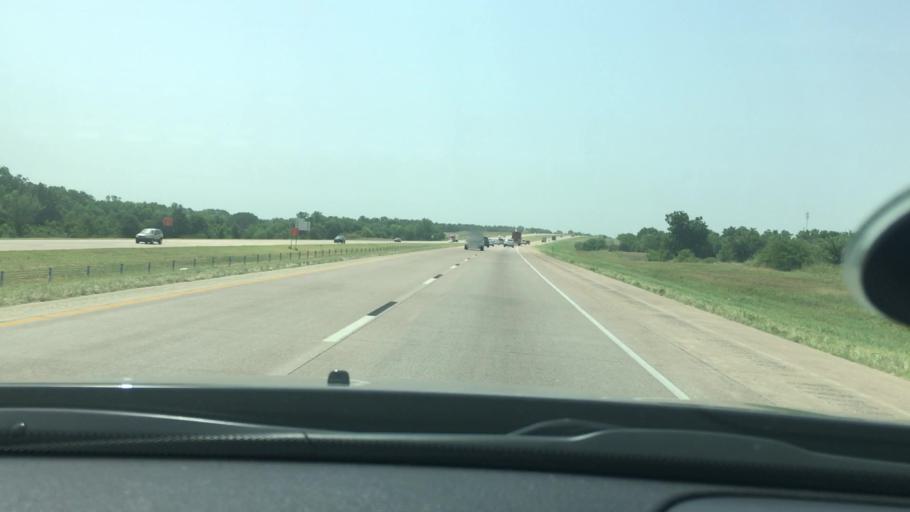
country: US
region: Oklahoma
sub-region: Garvin County
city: Pauls Valley
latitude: 34.6925
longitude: -97.2340
